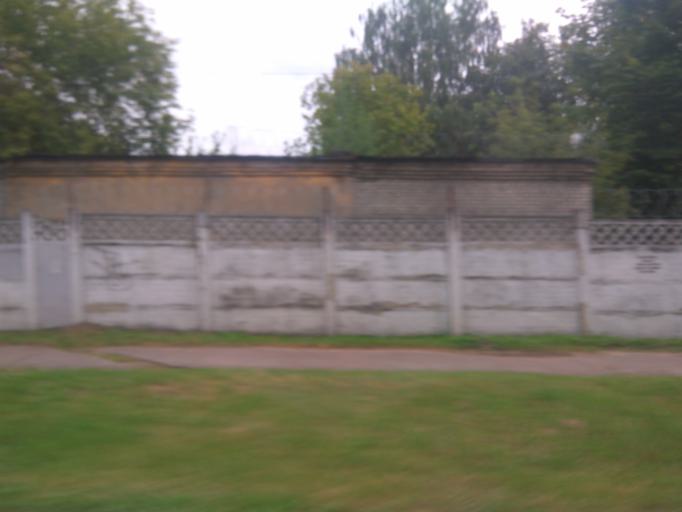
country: RU
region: Moskovskaya
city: Lyubertsy
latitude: 55.6999
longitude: 37.8788
